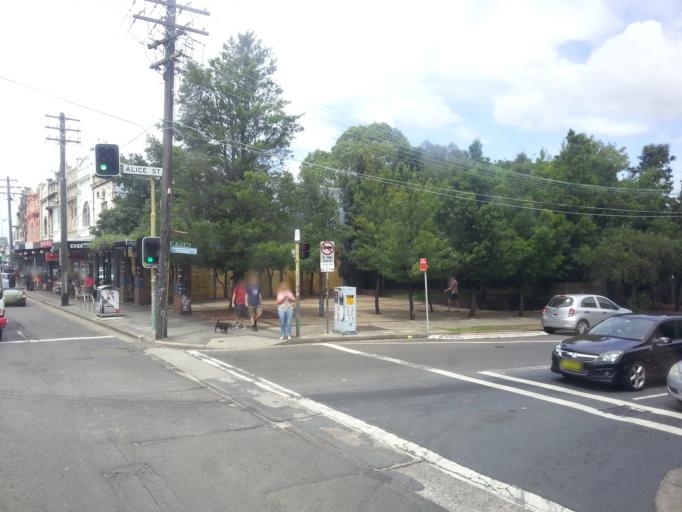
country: AU
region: New South Wales
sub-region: Marrickville
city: Newtown
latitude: -33.9029
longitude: 151.1794
